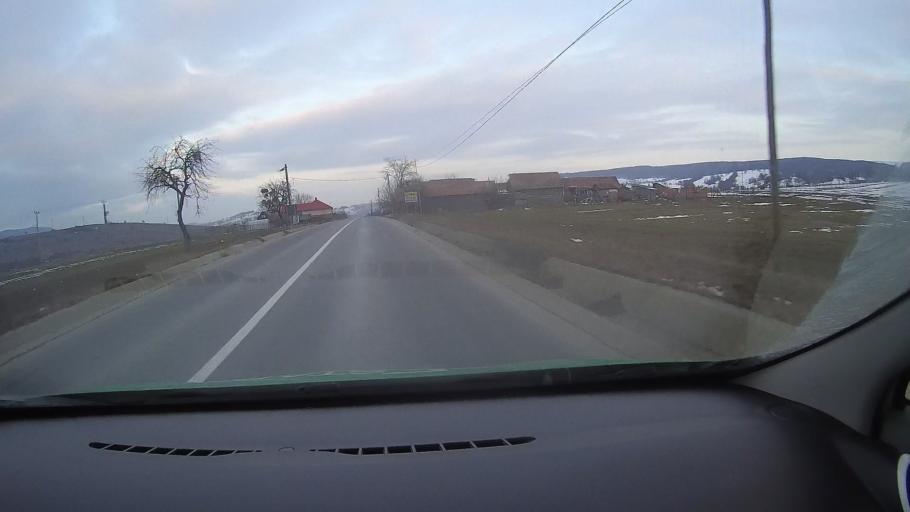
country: RO
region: Harghita
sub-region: Comuna Lupeni
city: Lupeni
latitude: 46.3565
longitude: 25.2123
